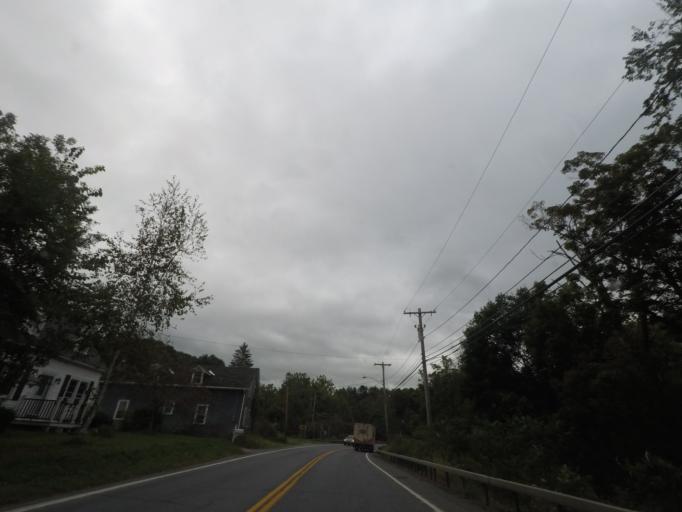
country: US
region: New York
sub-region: Rensselaer County
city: Hoosick Falls
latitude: 42.9304
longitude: -73.3508
